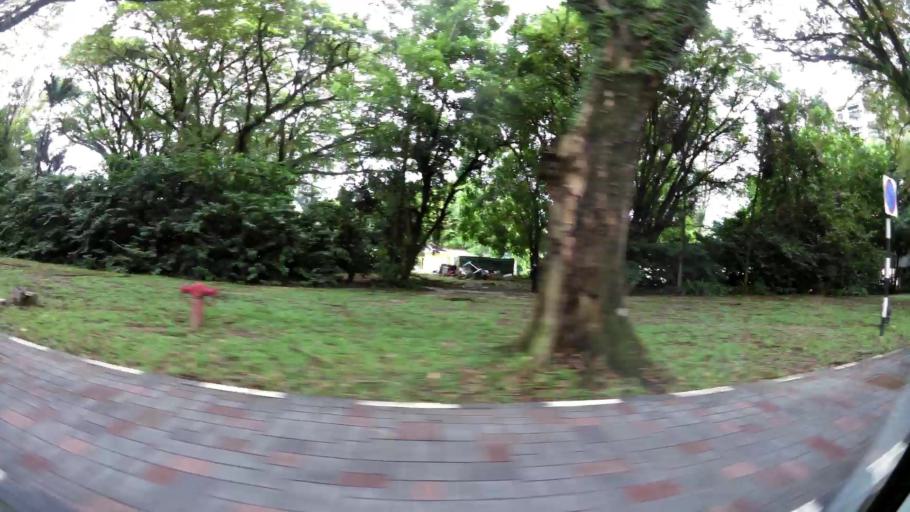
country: BN
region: Brunei and Muara
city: Bandar Seri Begawan
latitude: 4.8959
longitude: 114.9410
